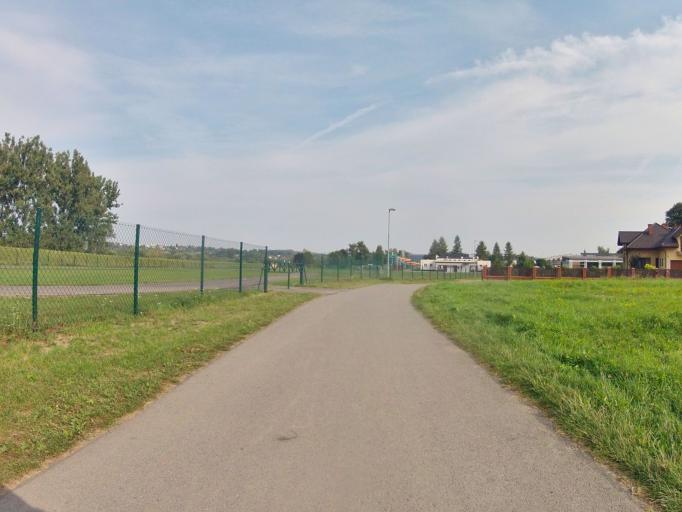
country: PL
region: Subcarpathian Voivodeship
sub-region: Powiat jasielski
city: Jaslo
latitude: 49.7417
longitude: 21.4563
